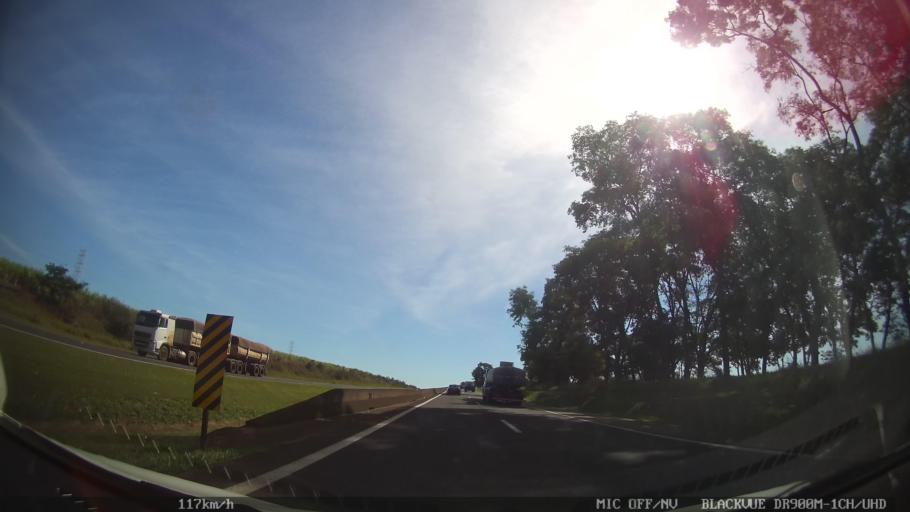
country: BR
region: Sao Paulo
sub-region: Porto Ferreira
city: Porto Ferreira
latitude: -21.8908
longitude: -47.4823
